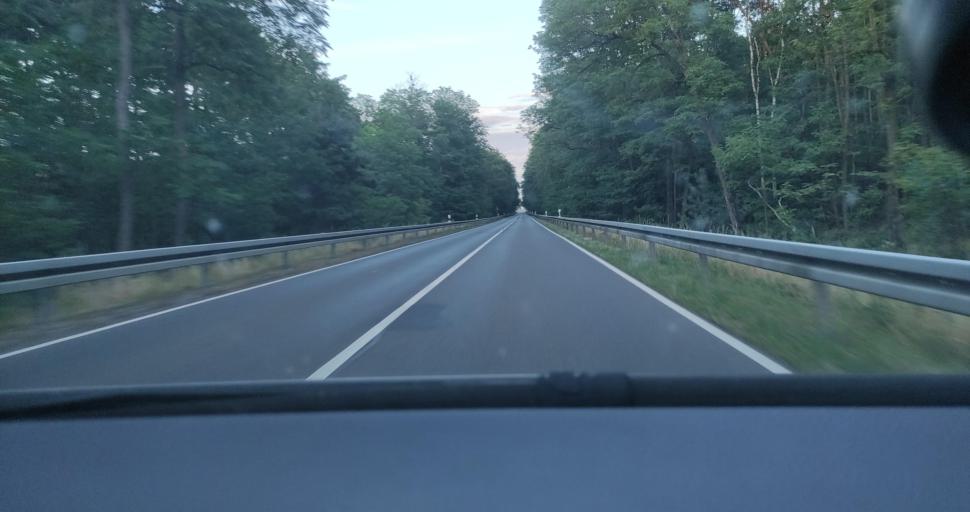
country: DE
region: Brandenburg
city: Heinersbruck
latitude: 51.7278
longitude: 14.5182
